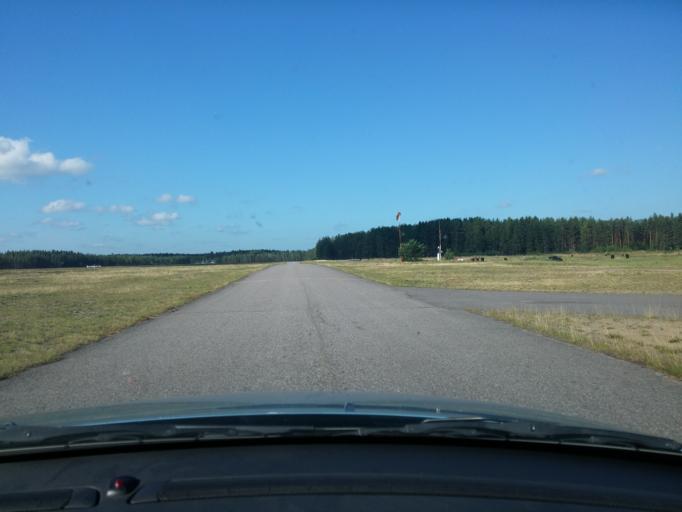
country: FI
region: Uusimaa
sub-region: Helsinki
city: Kaerkoelae
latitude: 60.7445
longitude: 24.1100
